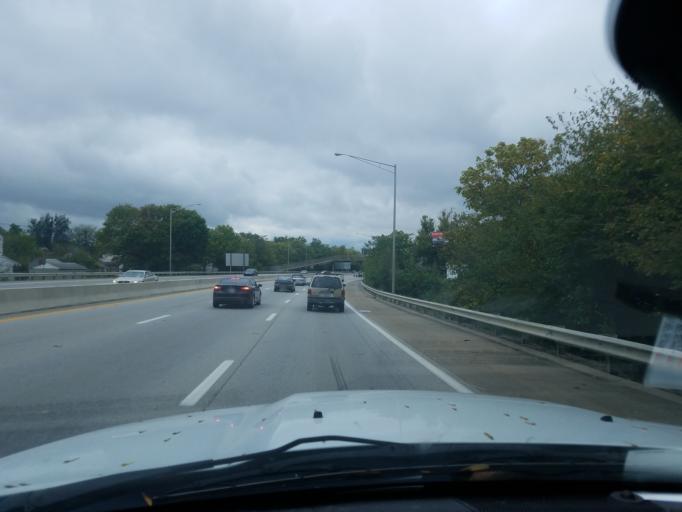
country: US
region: Kentucky
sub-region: Jefferson County
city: Louisville
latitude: 38.2653
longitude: -85.7766
